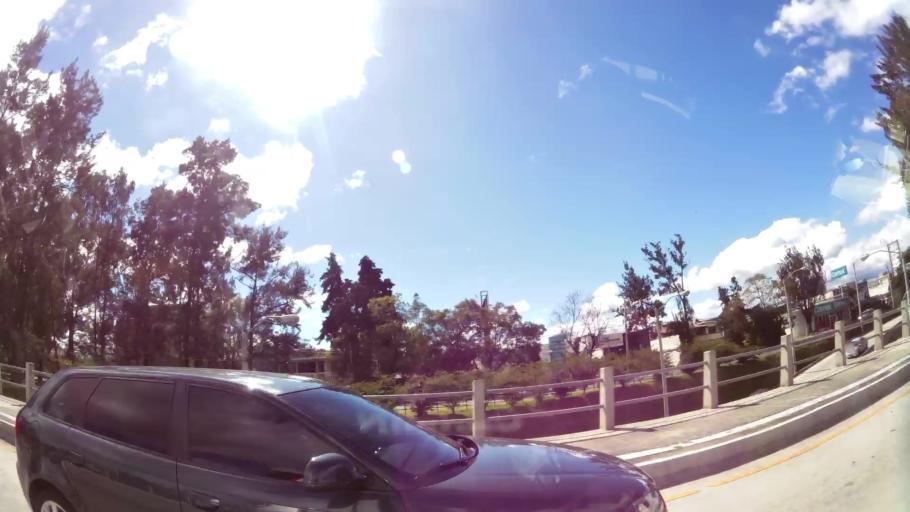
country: GT
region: Guatemala
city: Santa Catarina Pinula
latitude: 14.5979
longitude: -90.4970
